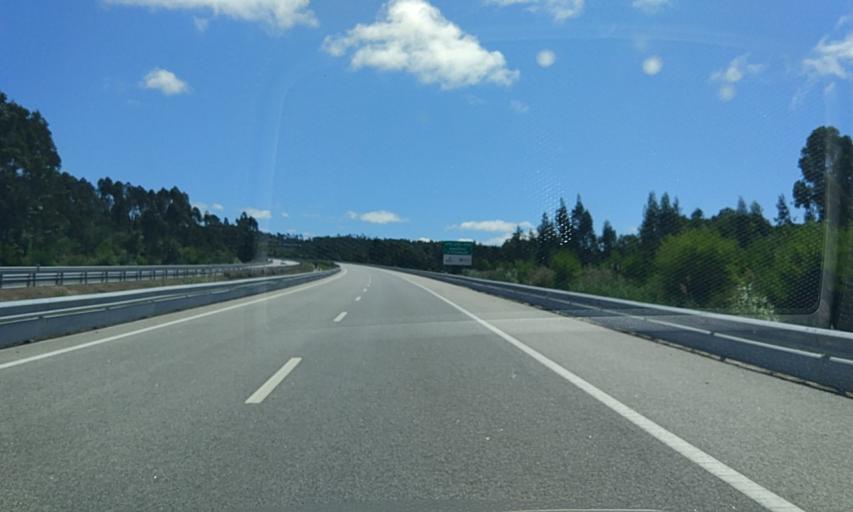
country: PT
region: Coimbra
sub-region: Figueira da Foz
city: Alhadas
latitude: 40.2057
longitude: -8.8104
